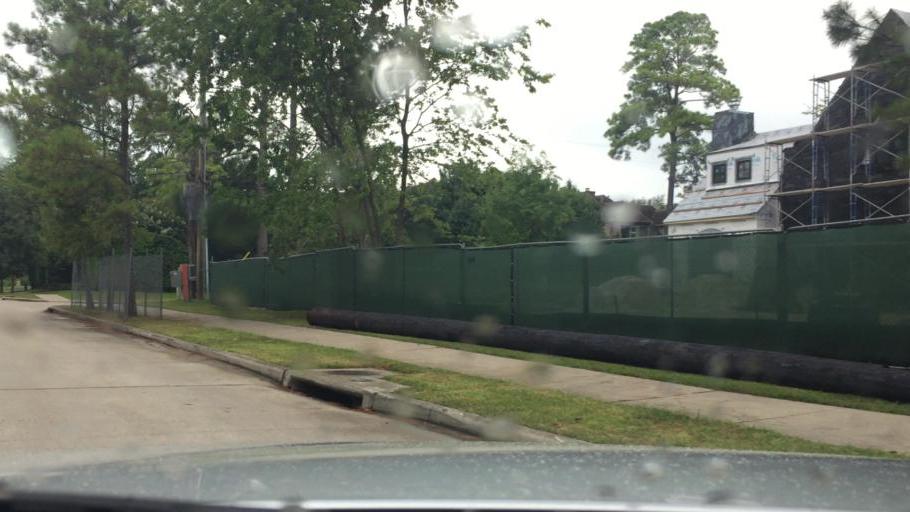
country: US
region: Texas
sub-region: Harris County
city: Piney Point Village
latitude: 29.7669
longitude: -95.5088
